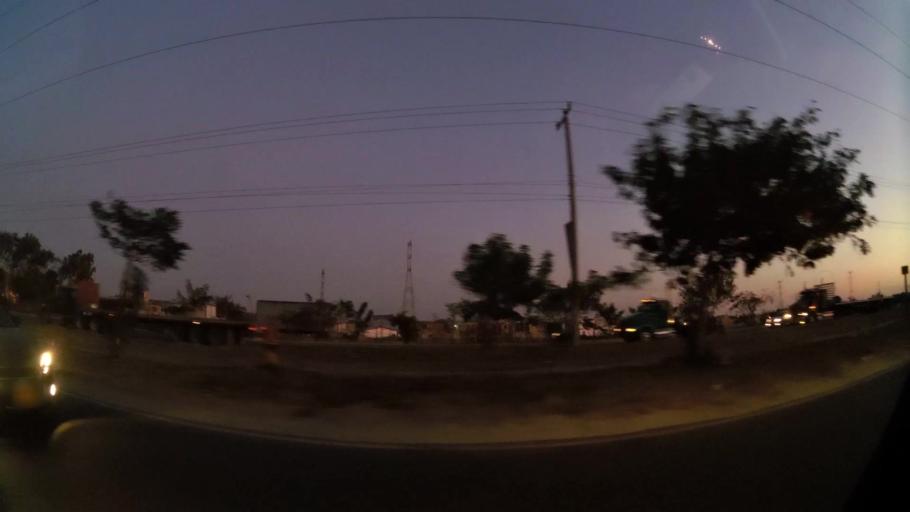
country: CO
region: Atlantico
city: Soledad
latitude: 10.9271
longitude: -74.7878
